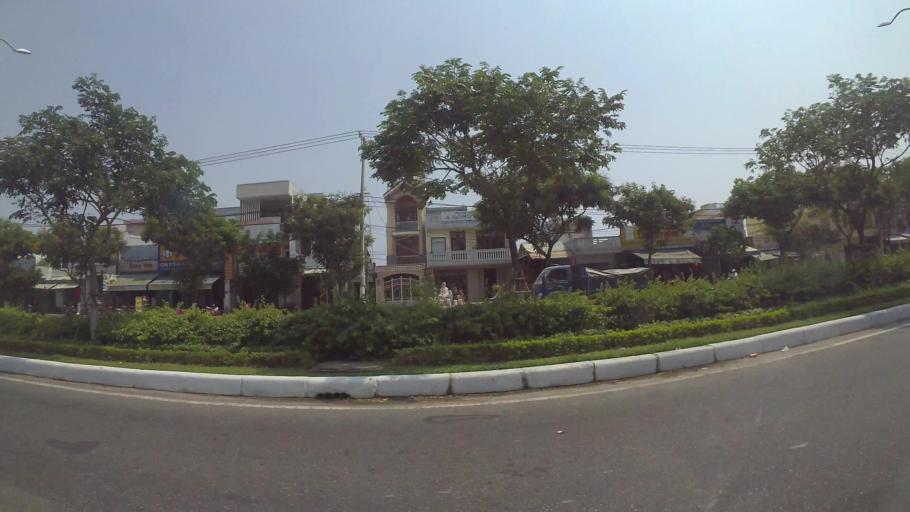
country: VN
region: Da Nang
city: Ngu Hanh Son
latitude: 16.0113
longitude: 108.2565
